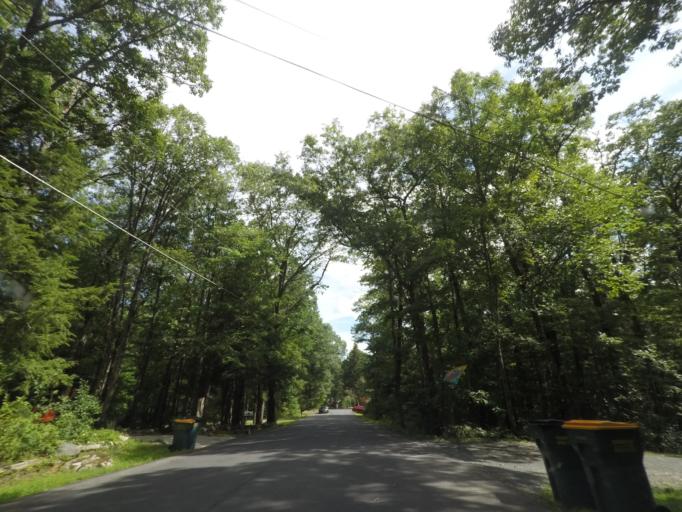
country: US
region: New York
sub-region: Rensselaer County
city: Averill Park
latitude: 42.6520
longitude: -73.5499
